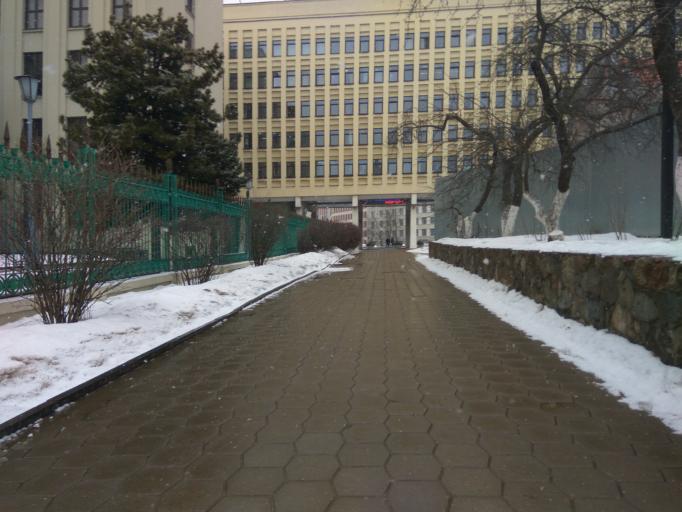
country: BY
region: Minsk
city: Minsk
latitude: 53.8962
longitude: 27.5468
